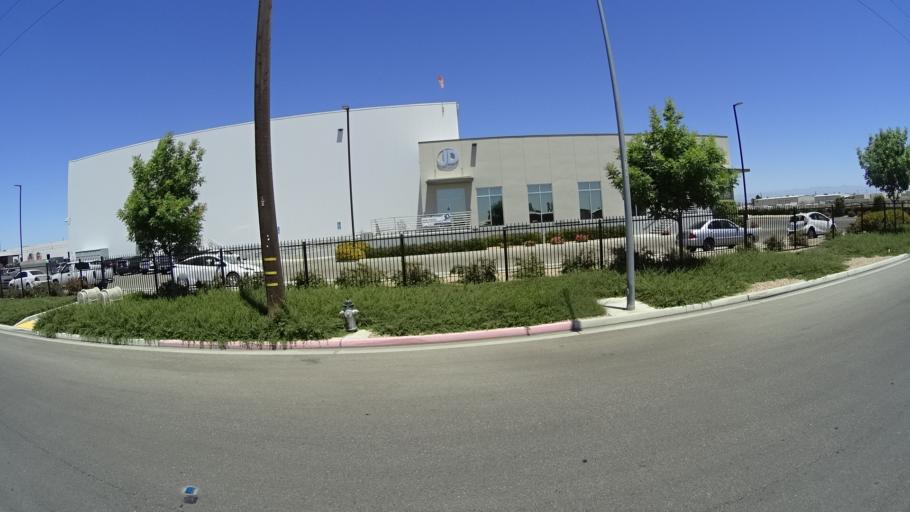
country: US
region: California
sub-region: Fresno County
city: Fresno
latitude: 36.6960
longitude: -119.7420
